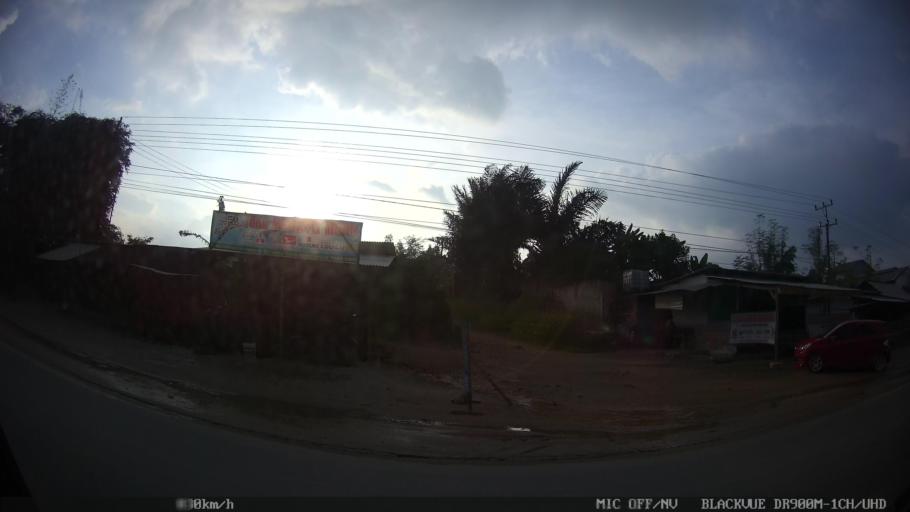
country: ID
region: Lampung
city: Panjang
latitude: -5.4107
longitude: 105.3471
